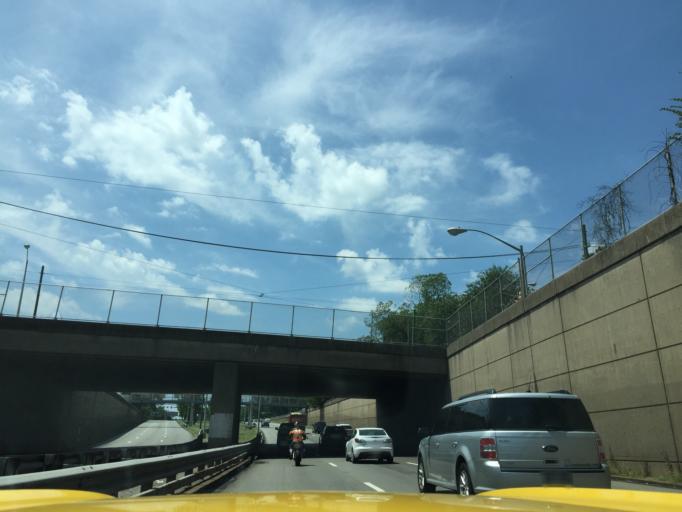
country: US
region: Pennsylvania
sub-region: Montgomery County
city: Rockledge
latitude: 40.0317
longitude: -75.0846
